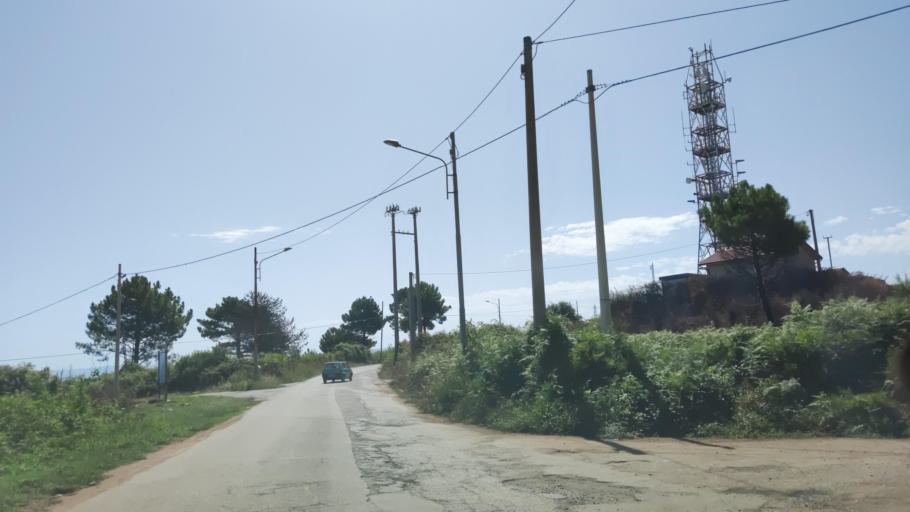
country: IT
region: Calabria
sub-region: Provincia di Reggio Calabria
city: Seminara
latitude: 38.3451
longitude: 15.8425
